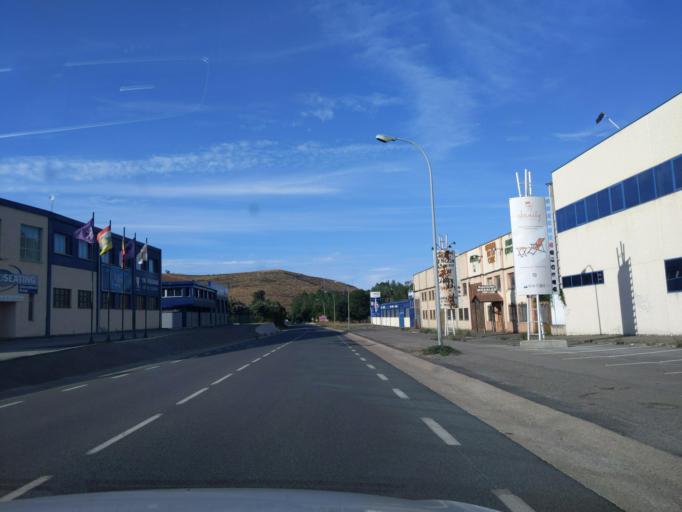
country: ES
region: La Rioja
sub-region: Provincia de La Rioja
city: Ezcaray
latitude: 42.3346
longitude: -3.0116
